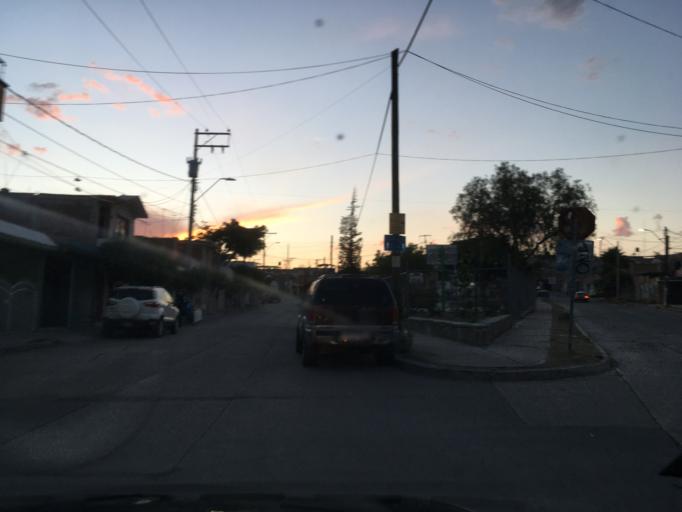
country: MX
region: Guanajuato
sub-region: Leon
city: San Jose de Duran (Los Troncoso)
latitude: 21.0819
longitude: -101.6320
